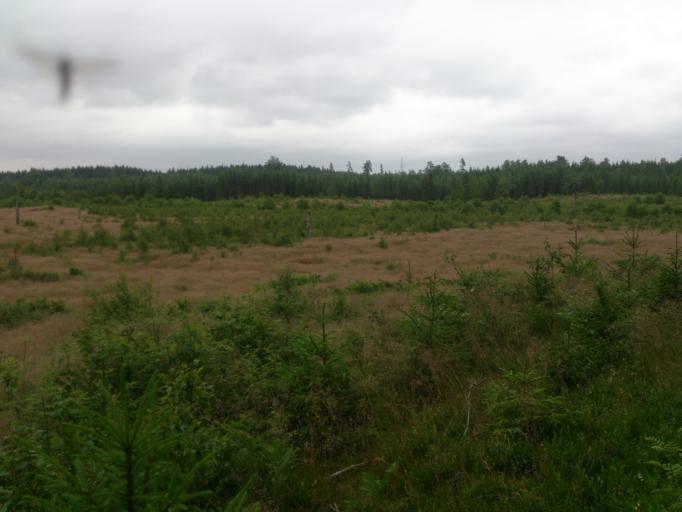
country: SE
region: Vaestra Goetaland
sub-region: Ulricehamns Kommun
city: Ulricehamn
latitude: 57.9585
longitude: 13.5470
